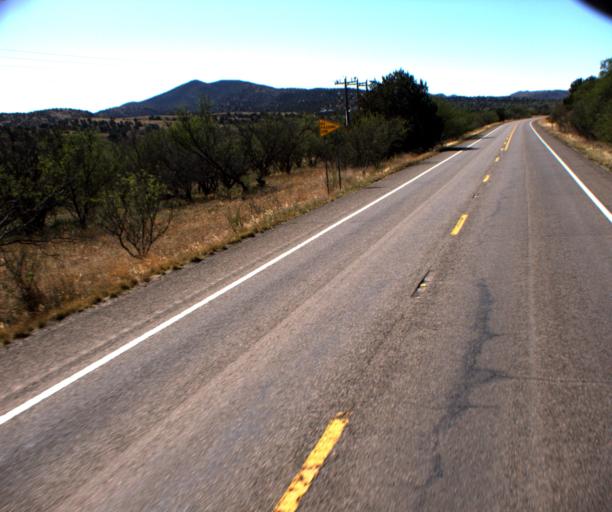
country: US
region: Arizona
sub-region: Santa Cruz County
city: Rio Rico
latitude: 31.6392
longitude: -110.7138
